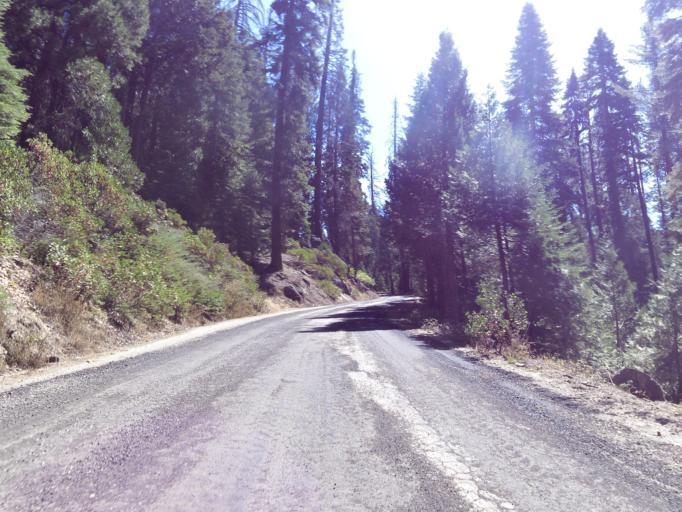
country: US
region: California
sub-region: Madera County
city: Oakhurst
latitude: 37.4123
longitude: -119.5729
